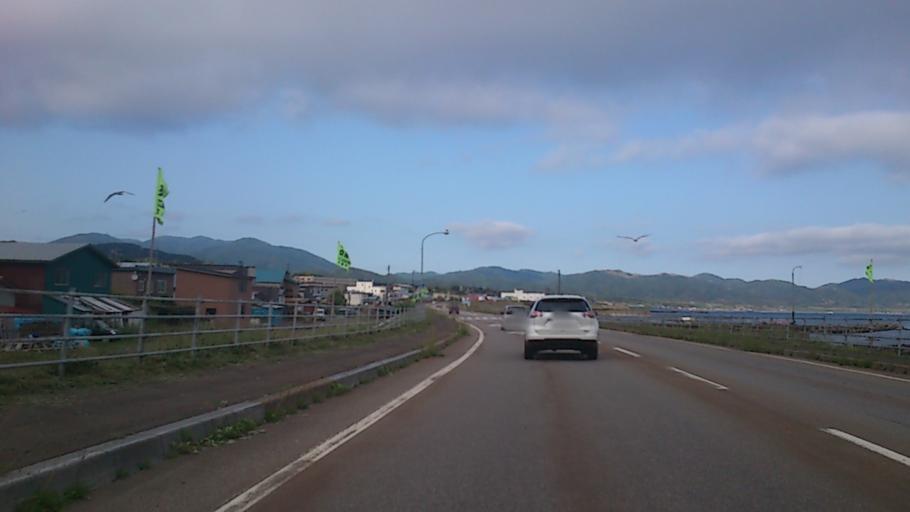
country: JP
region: Aomori
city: Shimokizukuri
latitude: 41.4246
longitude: 140.0961
